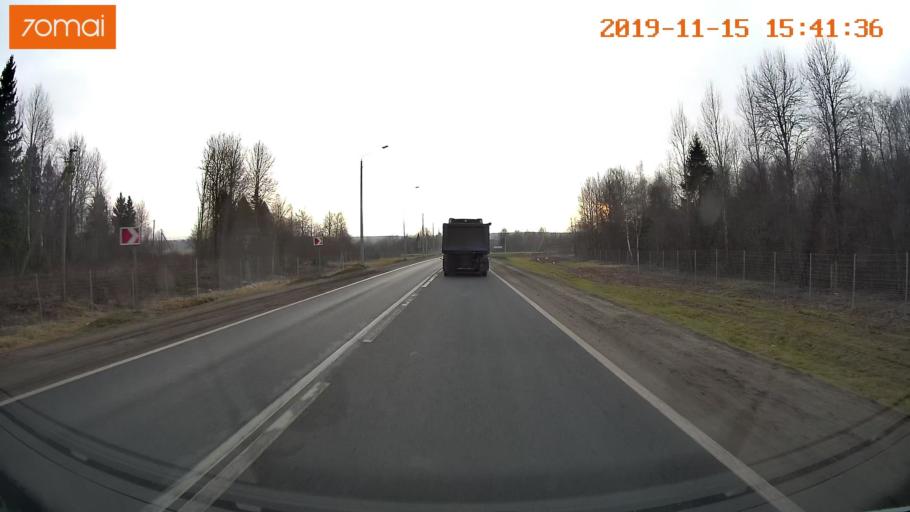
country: RU
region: Jaroslavl
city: Danilov
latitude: 57.9993
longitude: 40.0468
